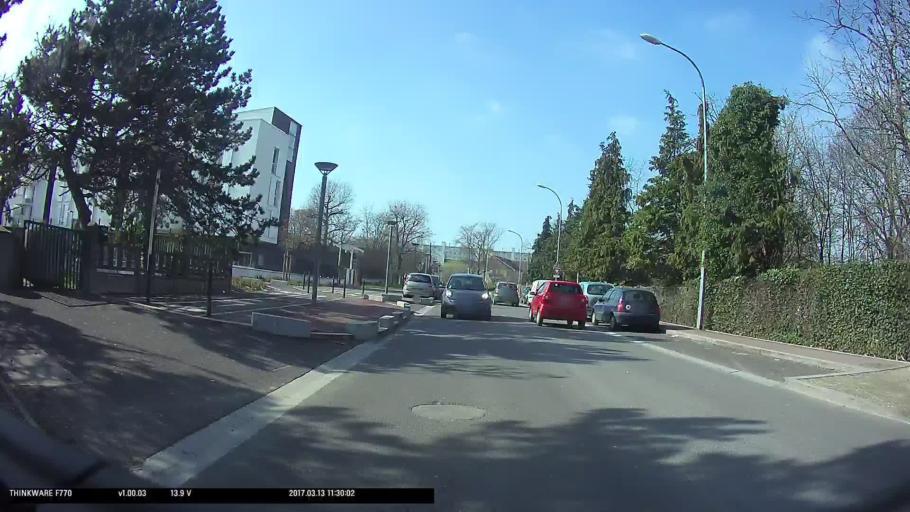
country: FR
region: Ile-de-France
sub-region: Departement de Seine-Saint-Denis
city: Noisy-le-Grand
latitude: 48.8482
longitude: 2.5776
